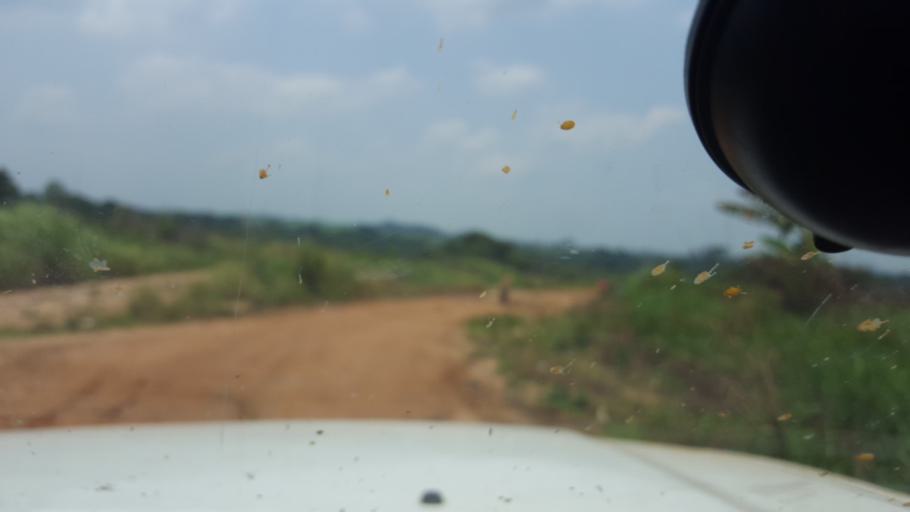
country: CD
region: Bandundu
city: Mushie
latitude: -3.7436
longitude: 16.6548
